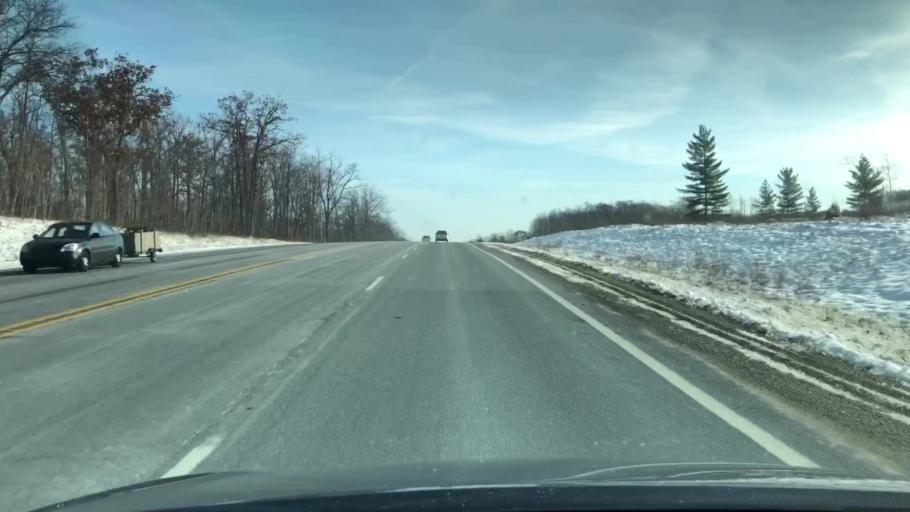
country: US
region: Michigan
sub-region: Crawford County
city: Grayling
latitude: 44.7003
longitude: -84.8855
